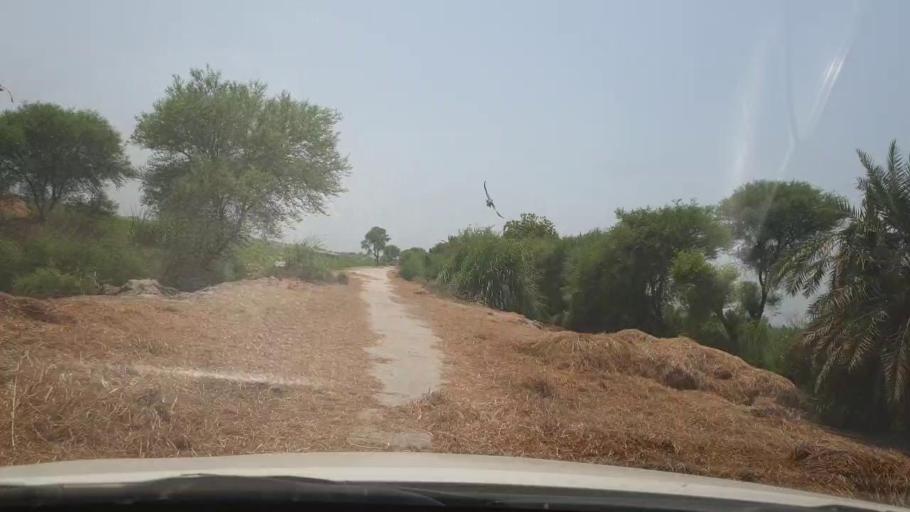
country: PK
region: Sindh
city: Shikarpur
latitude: 28.0800
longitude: 68.5513
